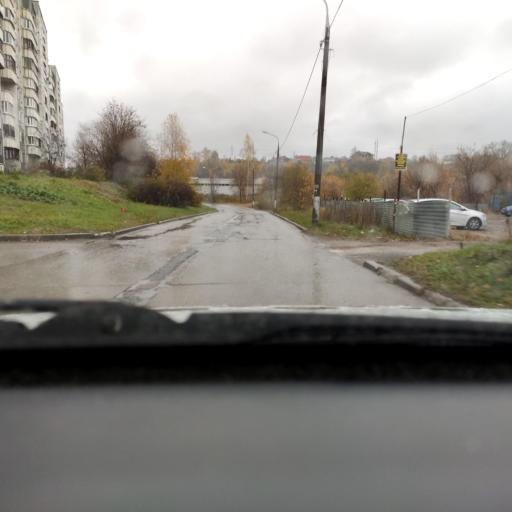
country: RU
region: Perm
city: Perm
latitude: 58.0093
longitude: 56.3136
